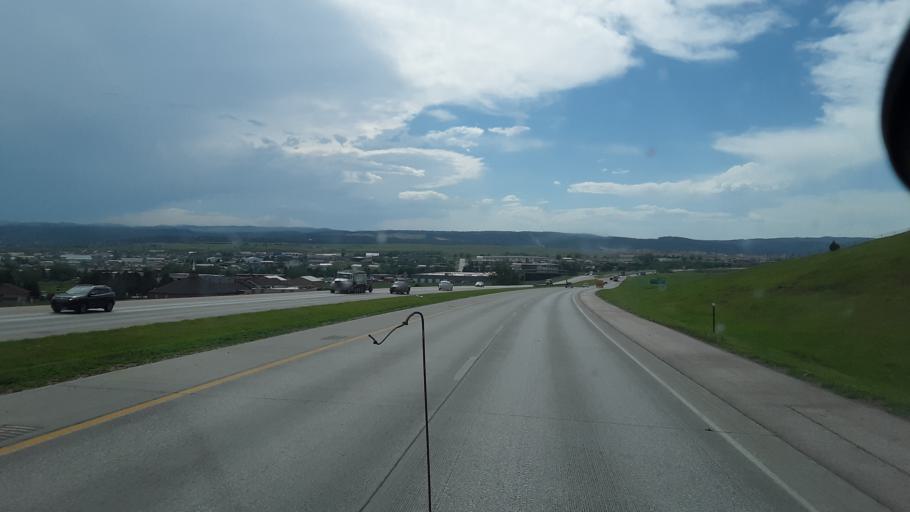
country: US
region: South Dakota
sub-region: Pennington County
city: Rapid City
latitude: 44.1063
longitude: -103.2494
